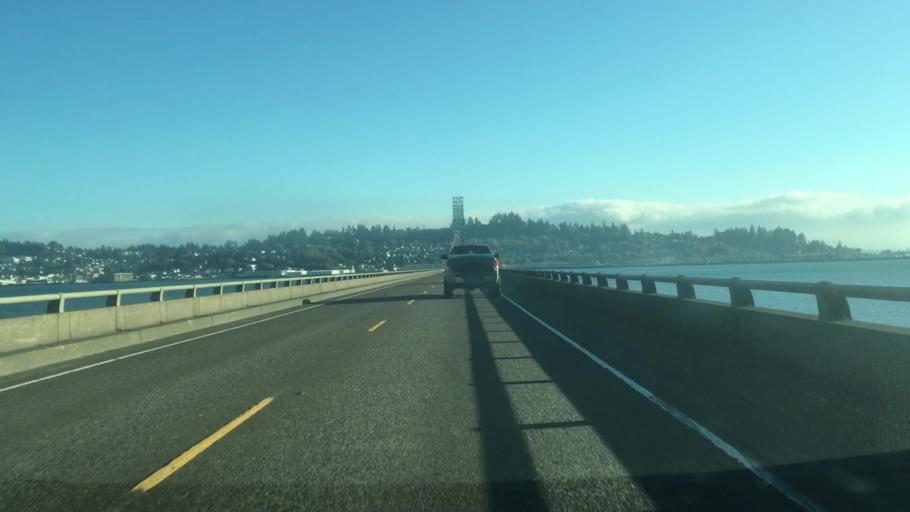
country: US
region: Oregon
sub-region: Clatsop County
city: Astoria
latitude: 46.2060
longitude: -123.8573
